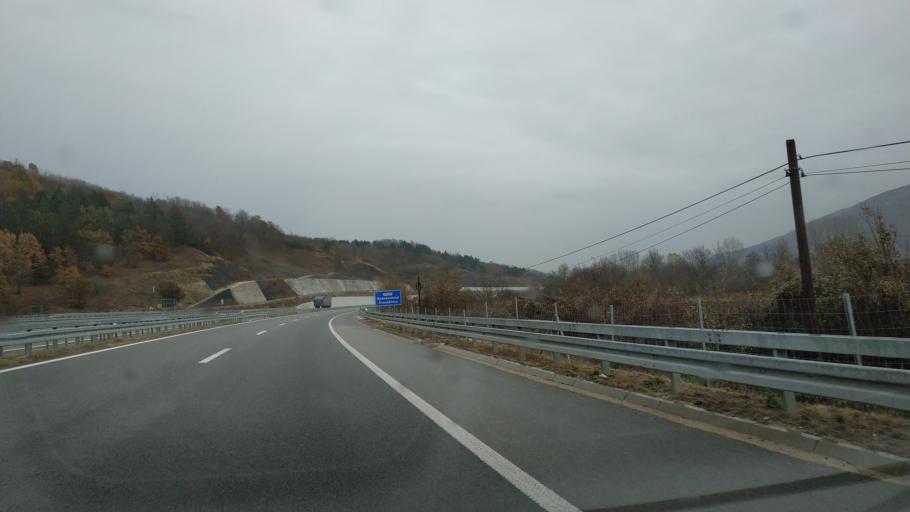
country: RS
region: Central Serbia
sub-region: Pirotski Okrug
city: Bela Palanka
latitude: 43.2334
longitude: 22.4520
